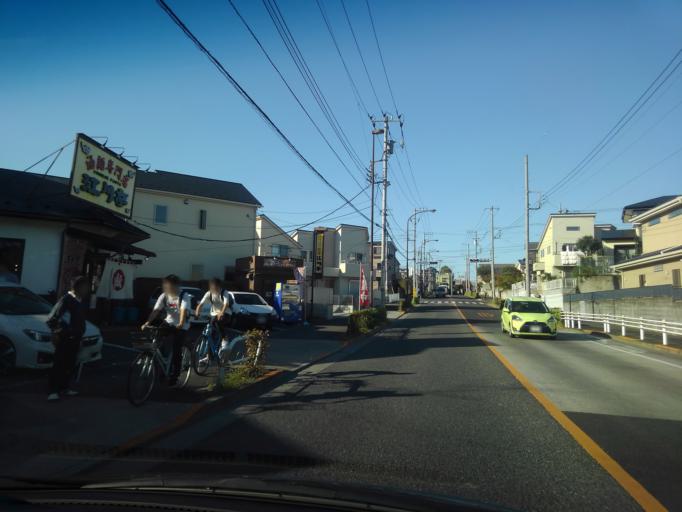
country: JP
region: Tokyo
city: Chofugaoka
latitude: 35.6781
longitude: 139.5389
